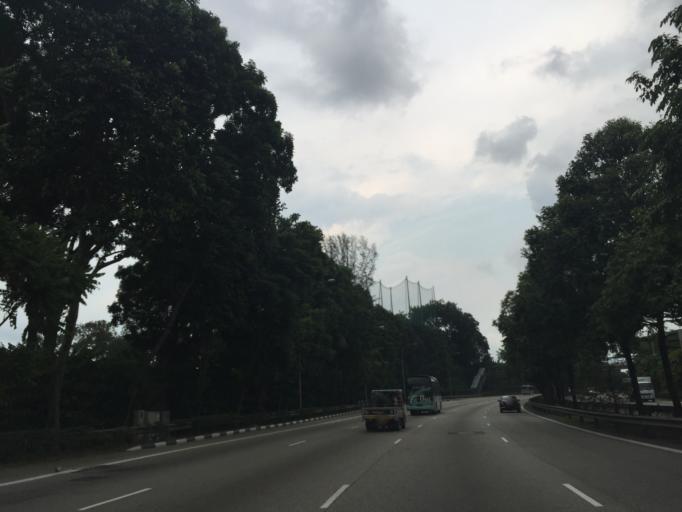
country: SG
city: Singapore
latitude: 1.3273
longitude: 103.7379
